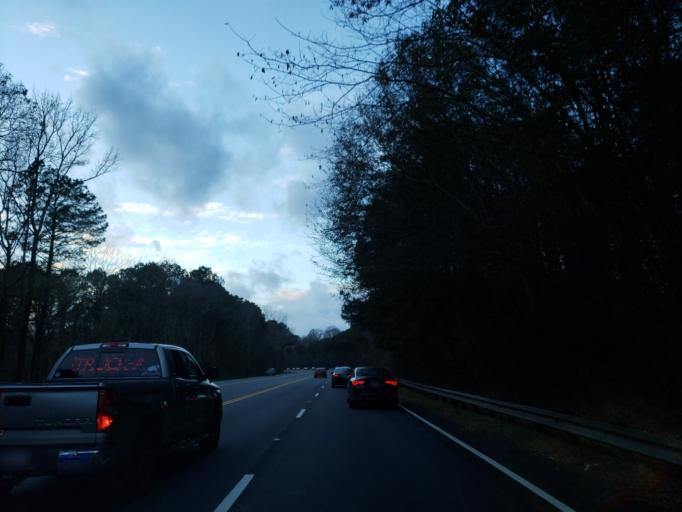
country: US
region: Georgia
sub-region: Fulton County
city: College Park
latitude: 33.6575
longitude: -84.5224
